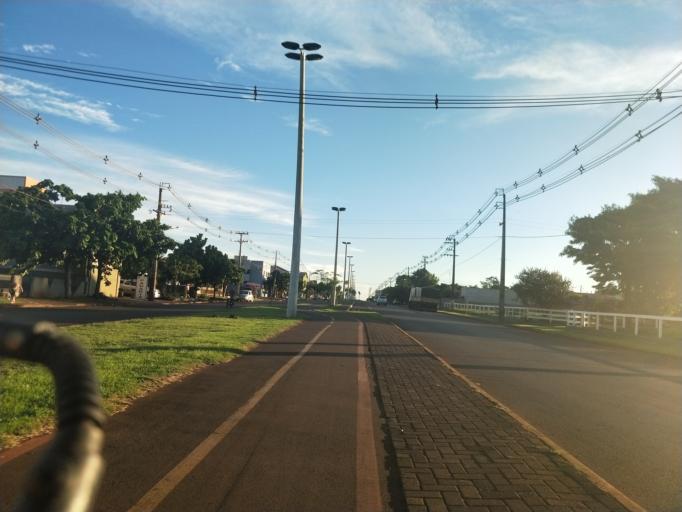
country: BR
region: Parana
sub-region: Marechal Candido Rondon
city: Marechal Candido Rondon
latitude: -24.5468
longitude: -54.0445
